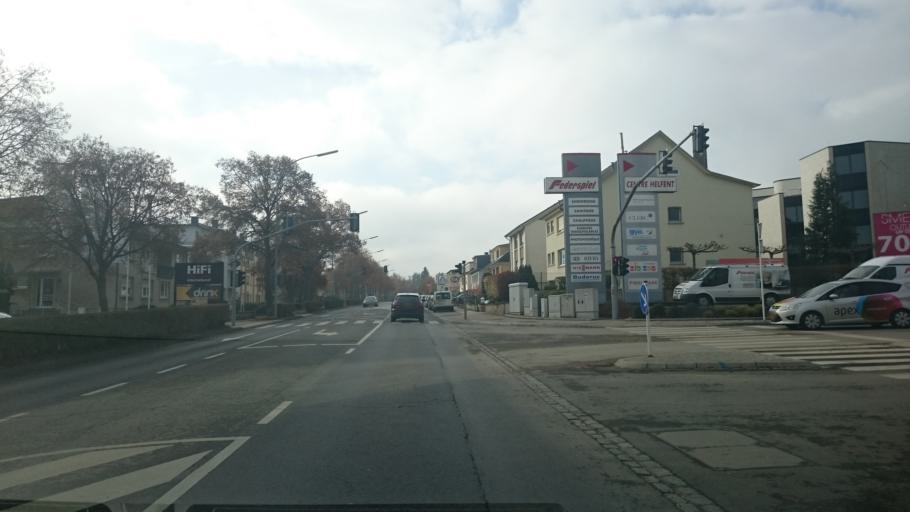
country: LU
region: Luxembourg
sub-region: Canton de Luxembourg
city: Strassen
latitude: 49.6033
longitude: 6.0746
